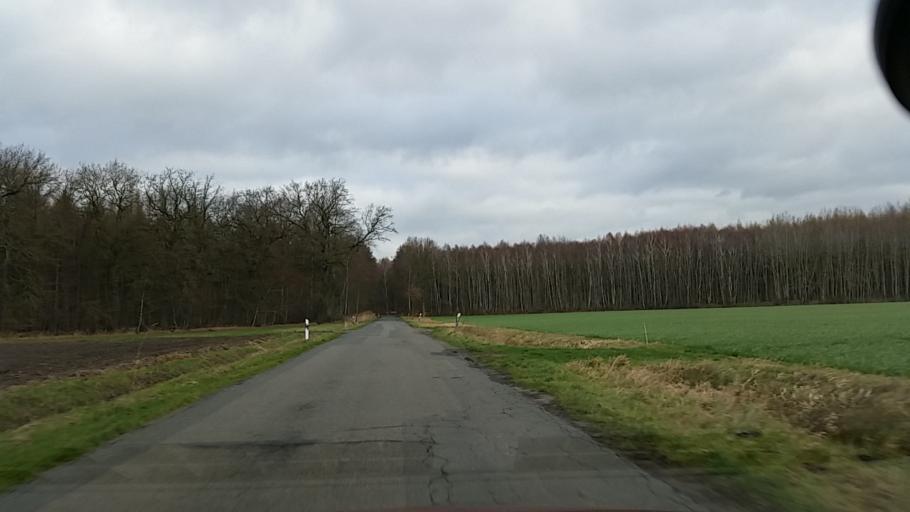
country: DE
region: Lower Saxony
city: Luder
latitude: 52.7673
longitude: 10.6664
